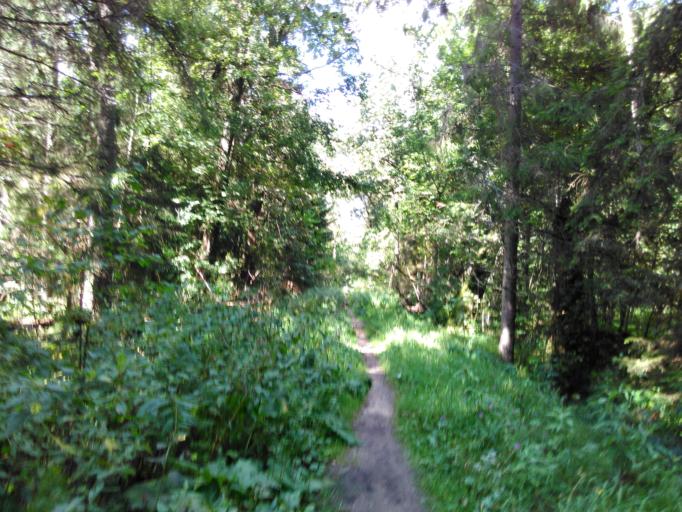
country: RU
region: Tverskaya
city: Konakovo
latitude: 56.6857
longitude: 36.7039
